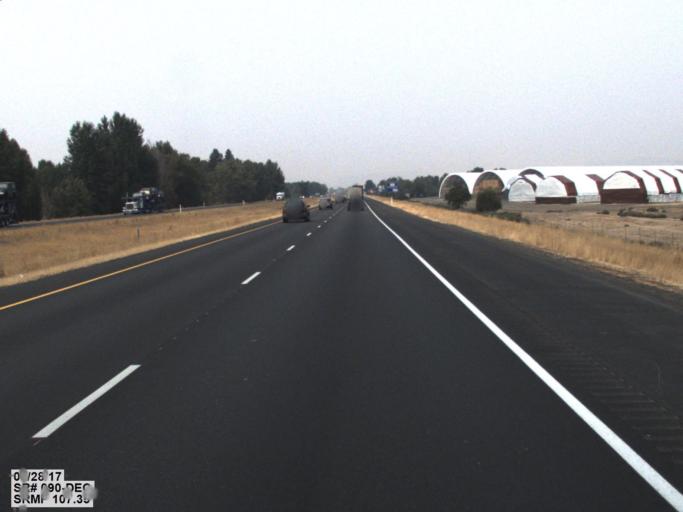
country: US
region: Washington
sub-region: Kittitas County
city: Ellensburg
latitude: 46.9917
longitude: -120.5732
